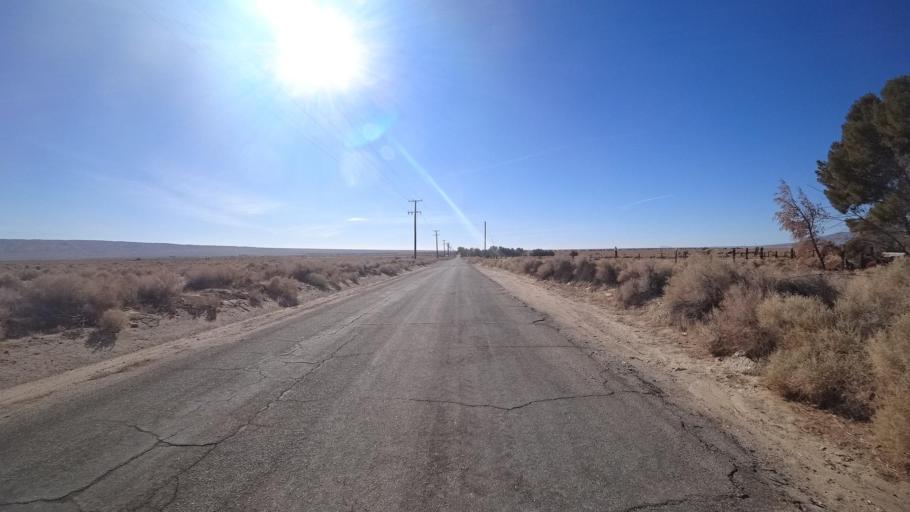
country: US
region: California
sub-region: Kern County
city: California City
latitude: 35.3070
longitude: -117.9504
